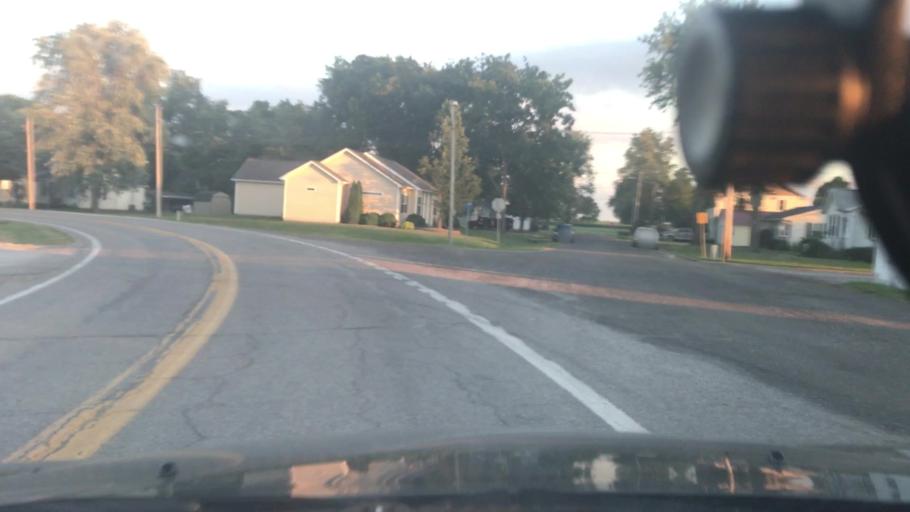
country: US
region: Illinois
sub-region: Washington County
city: Okawville
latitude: 38.3926
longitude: -89.4923
